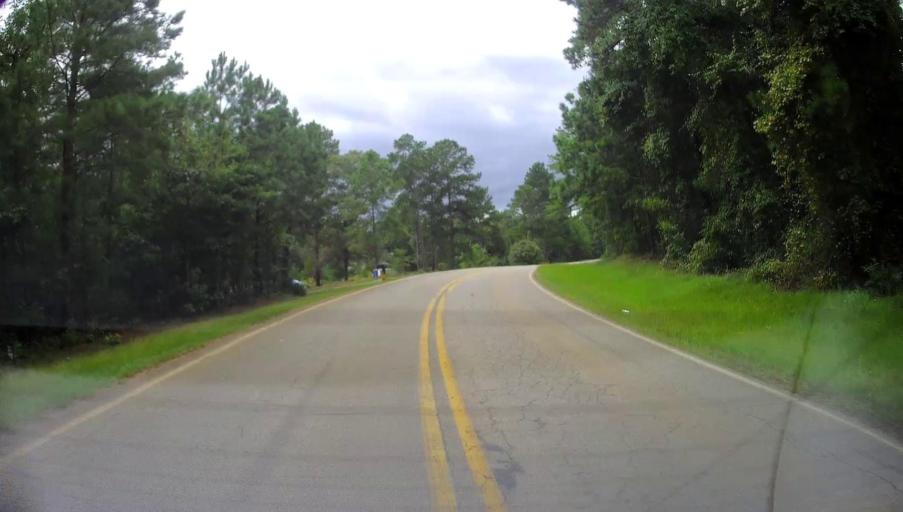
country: US
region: Georgia
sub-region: Twiggs County
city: Jeffersonville
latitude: 32.7602
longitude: -83.4890
